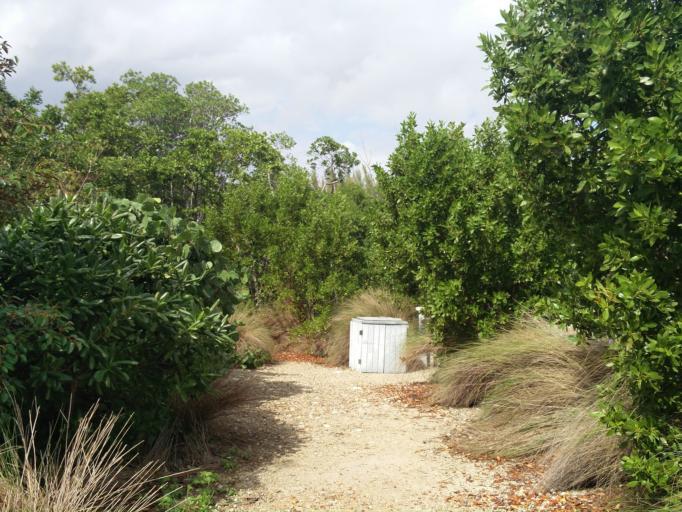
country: US
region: Florida
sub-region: Broward County
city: Dania Beach
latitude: 26.0406
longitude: -80.1177
